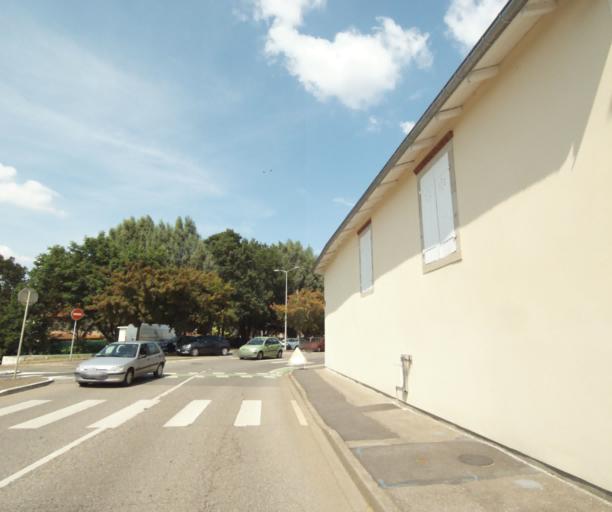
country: FR
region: Lorraine
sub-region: Departement de Meurthe-et-Moselle
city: Luneville
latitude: 48.5946
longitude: 6.4869
